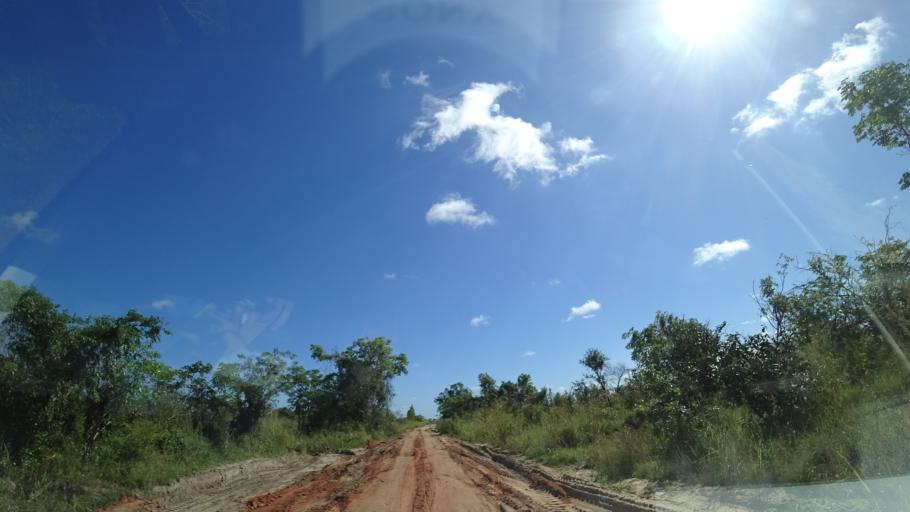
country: MZ
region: Sofala
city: Dondo
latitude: -19.2824
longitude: 34.6847
